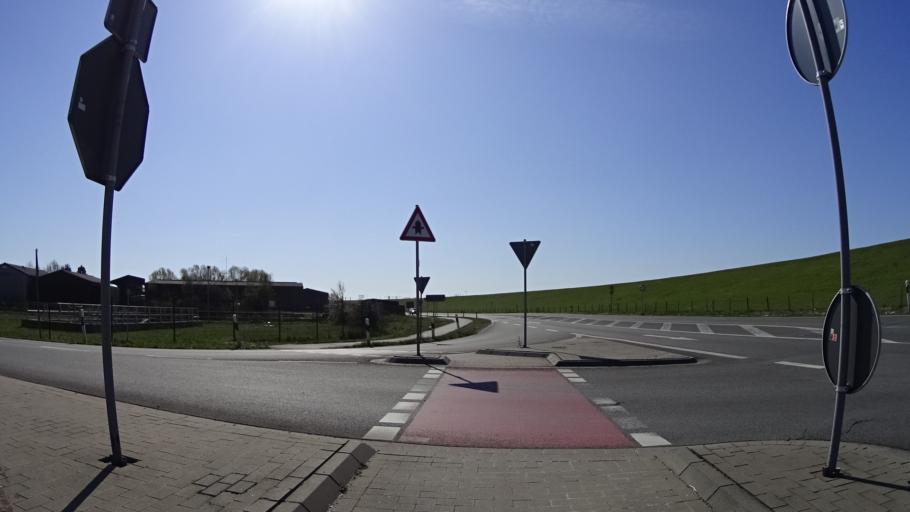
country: DE
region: Lower Saxony
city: Jemgum
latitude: 53.2367
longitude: 7.4084
